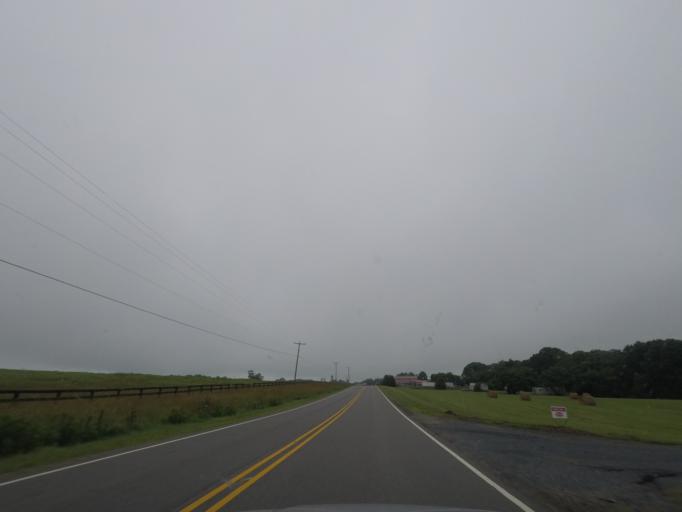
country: US
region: Virginia
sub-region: Fluvanna County
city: Weber City
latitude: 37.6111
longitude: -78.3827
